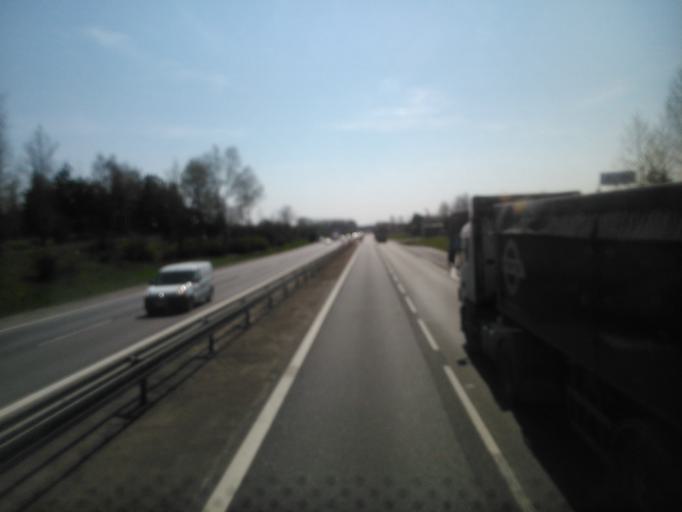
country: PL
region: Silesian Voivodeship
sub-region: Powiat czestochowski
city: Kamienica Polska
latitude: 50.6805
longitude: 19.1283
